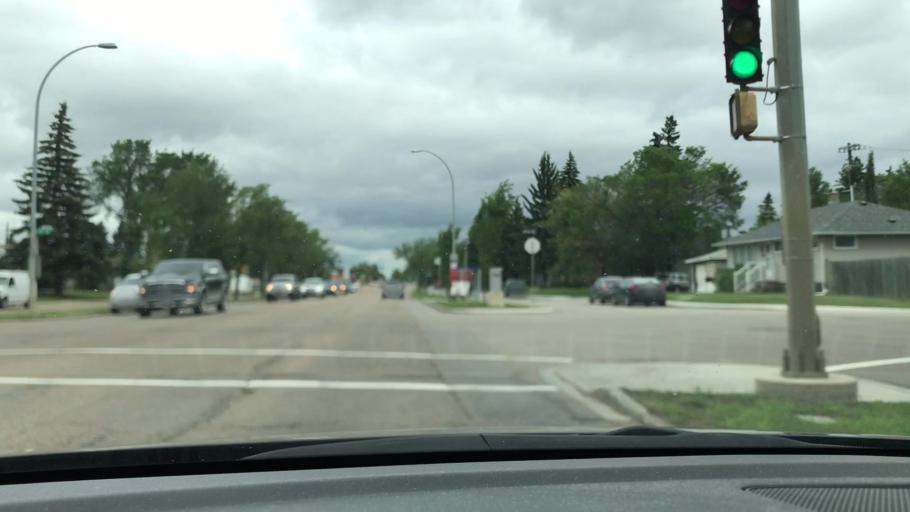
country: CA
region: Alberta
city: Edmonton
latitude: 53.5167
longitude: -113.5778
